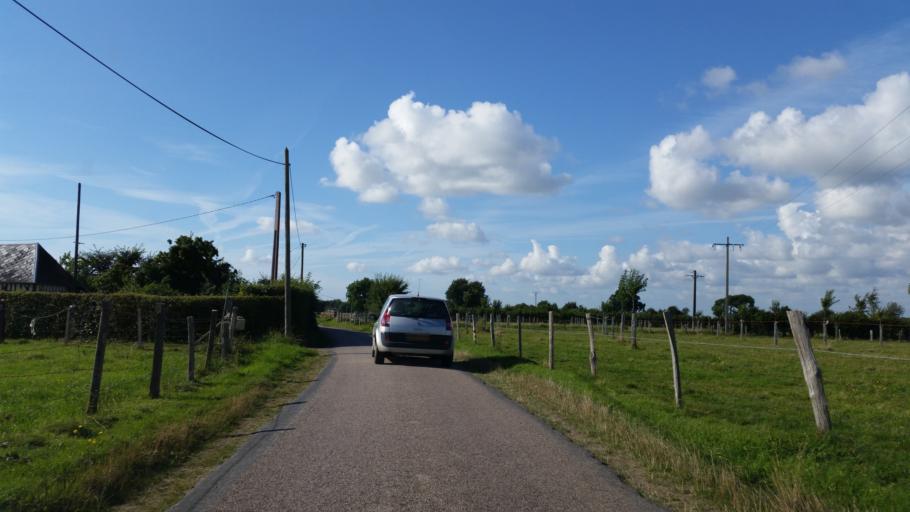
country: FR
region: Lower Normandy
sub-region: Departement du Calvados
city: Equemauville
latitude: 49.3827
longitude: 0.2277
